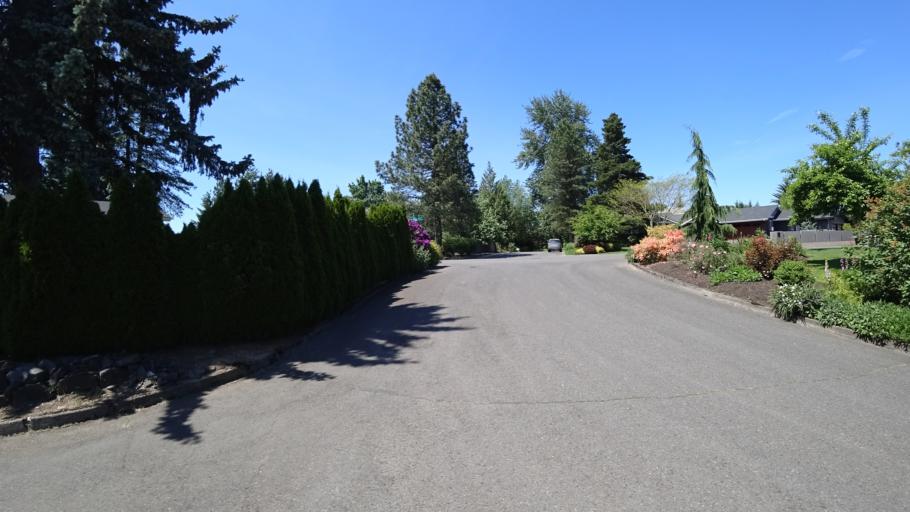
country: US
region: Oregon
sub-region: Washington County
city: Metzger
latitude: 45.4531
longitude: -122.7115
